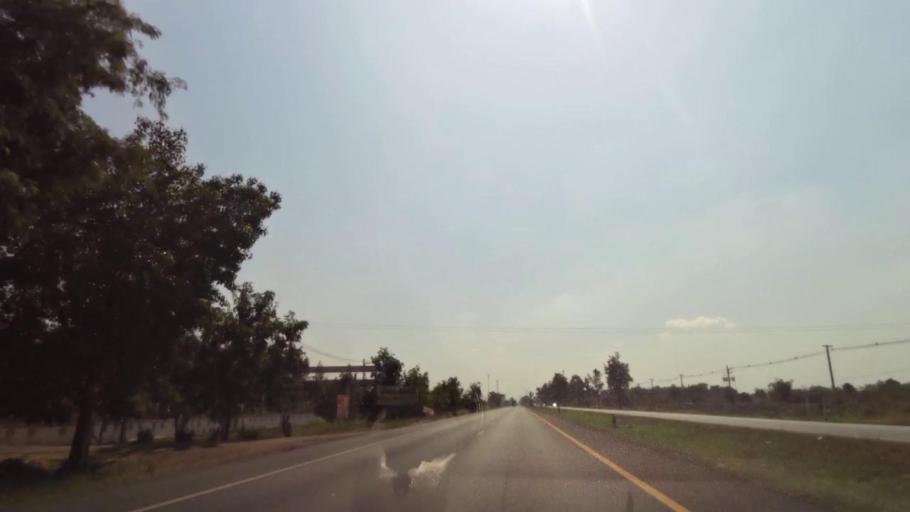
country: TH
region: Phichit
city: Bueng Na Rang
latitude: 16.2783
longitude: 100.1271
